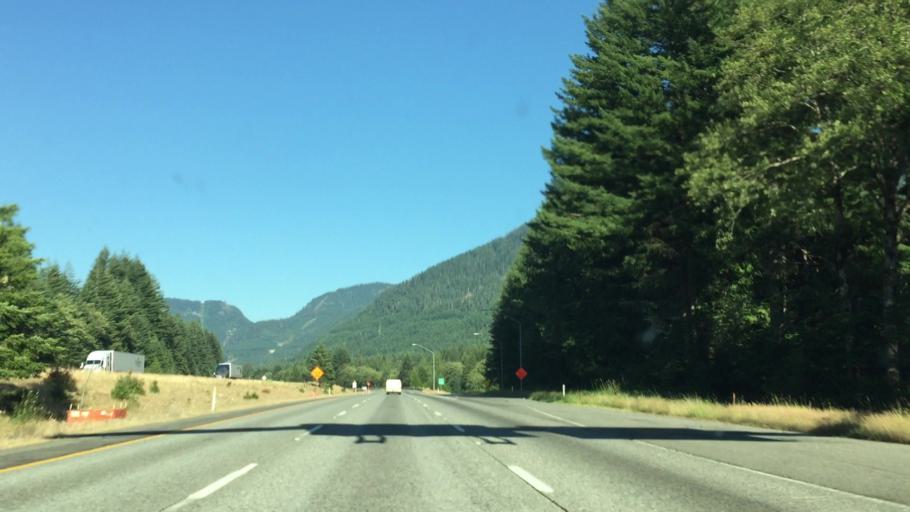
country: US
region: Washington
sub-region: King County
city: Tanner
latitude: 47.3958
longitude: -121.5325
